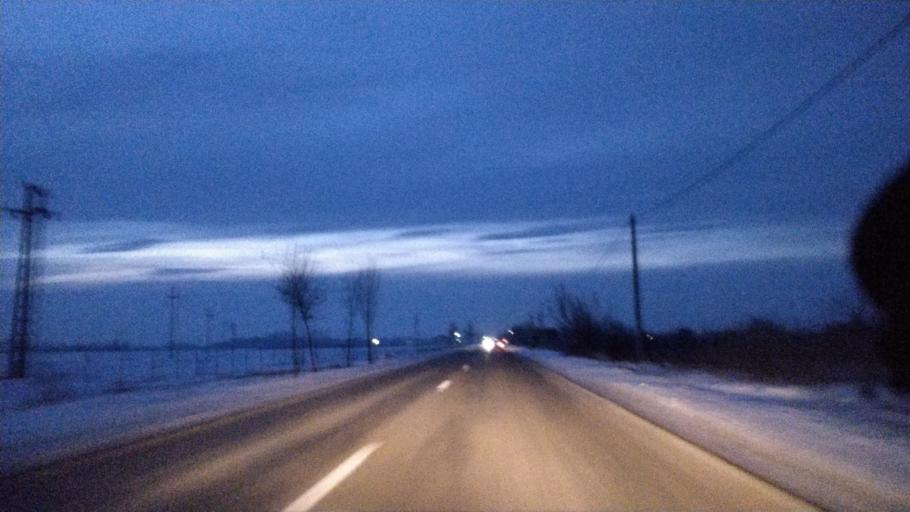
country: RO
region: Vrancea
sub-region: Comuna Rastoaca
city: Rastoaca
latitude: 45.6536
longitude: 27.3033
